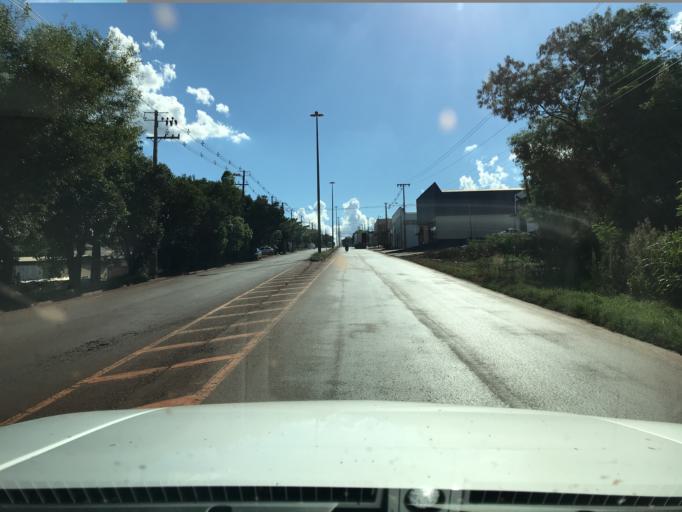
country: BR
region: Parana
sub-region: Palotina
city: Palotina
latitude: -24.2785
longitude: -53.8226
